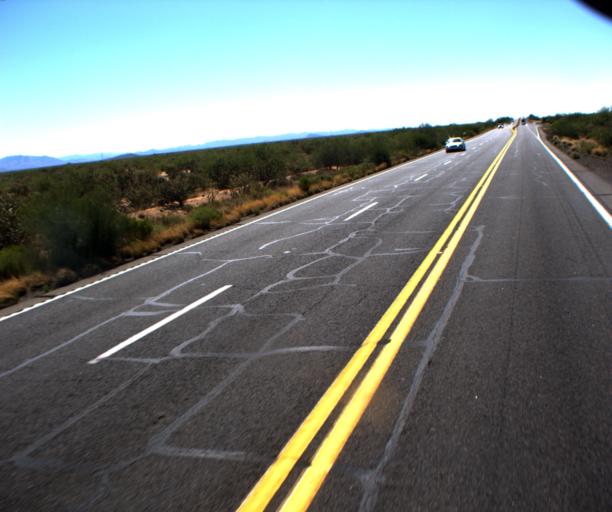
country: US
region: Arizona
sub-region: Yavapai County
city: Congress
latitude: 34.1279
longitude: -112.9570
